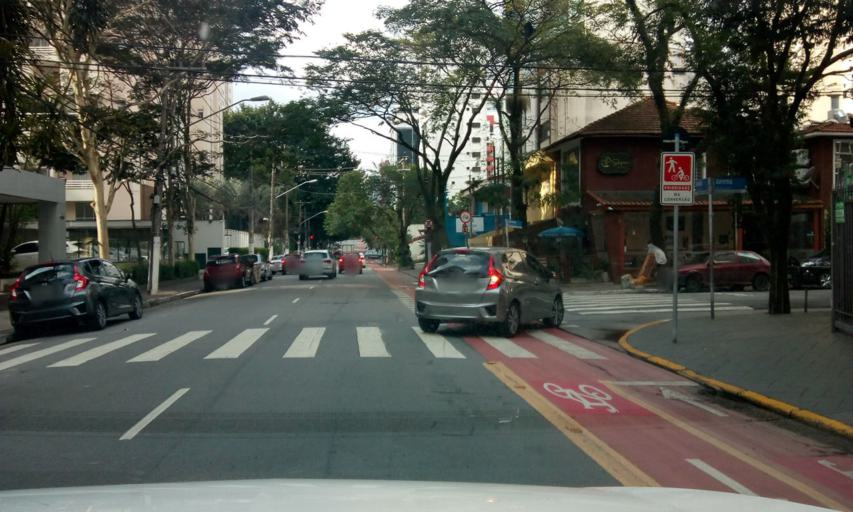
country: BR
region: Sao Paulo
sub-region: Sao Paulo
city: Sao Paulo
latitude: -23.6065
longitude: -46.6619
